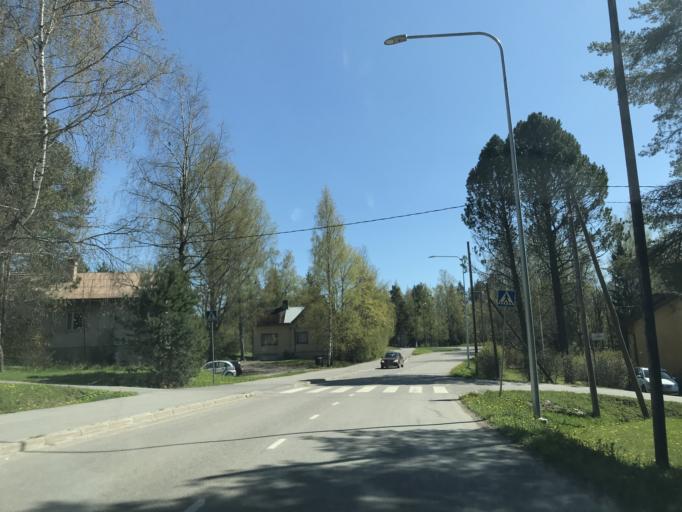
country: FI
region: Paijanne Tavastia
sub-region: Lahti
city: Orimattila
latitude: 60.8115
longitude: 25.7354
